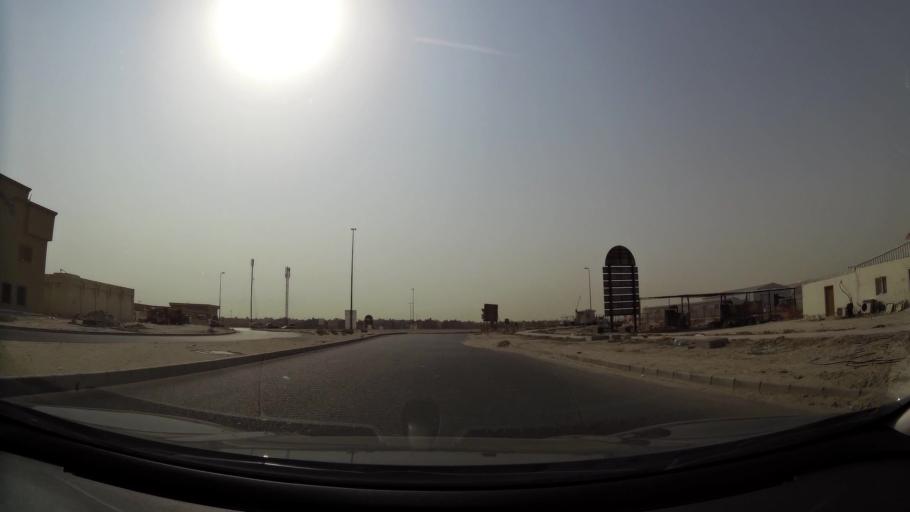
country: KW
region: Muhafazat al Jahra'
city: Al Jahra'
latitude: 29.3470
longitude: 47.7594
